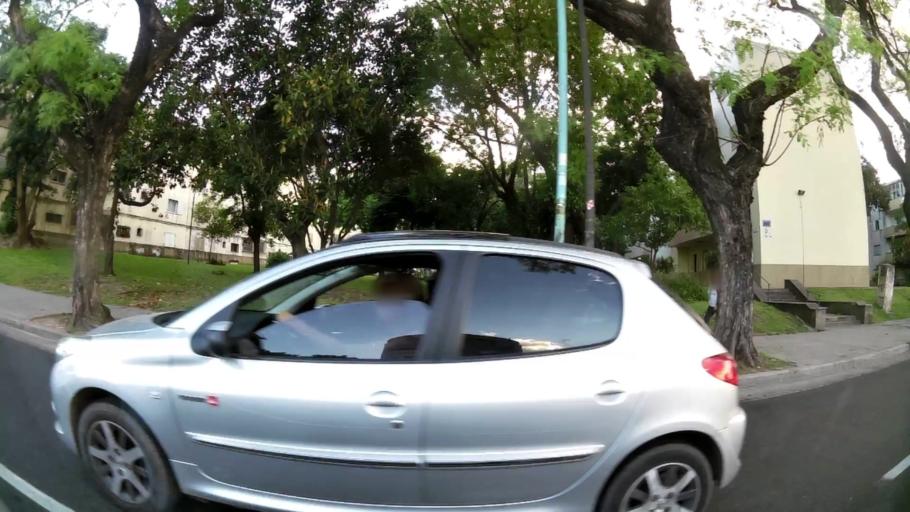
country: AR
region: Buenos Aires
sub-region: Partido de General San Martin
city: General San Martin
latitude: -34.5709
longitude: -58.5095
